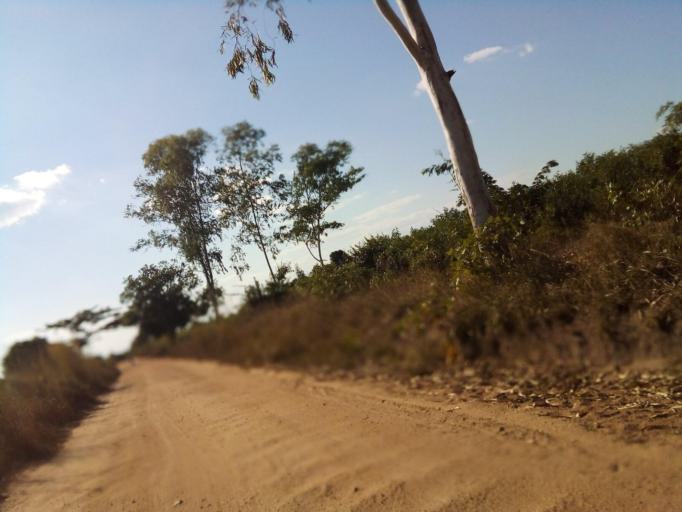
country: MZ
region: Zambezia
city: Quelimane
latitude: -17.5650
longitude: 36.6366
